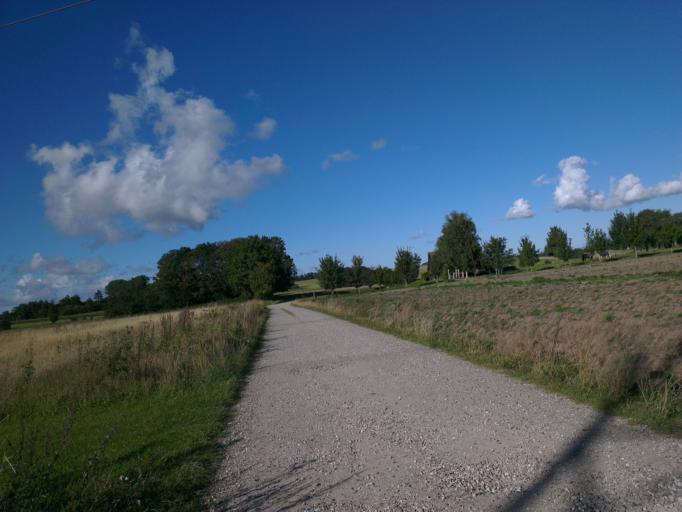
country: DK
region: Capital Region
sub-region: Frederikssund Kommune
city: Frederikssund
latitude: 55.7973
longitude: 12.0310
